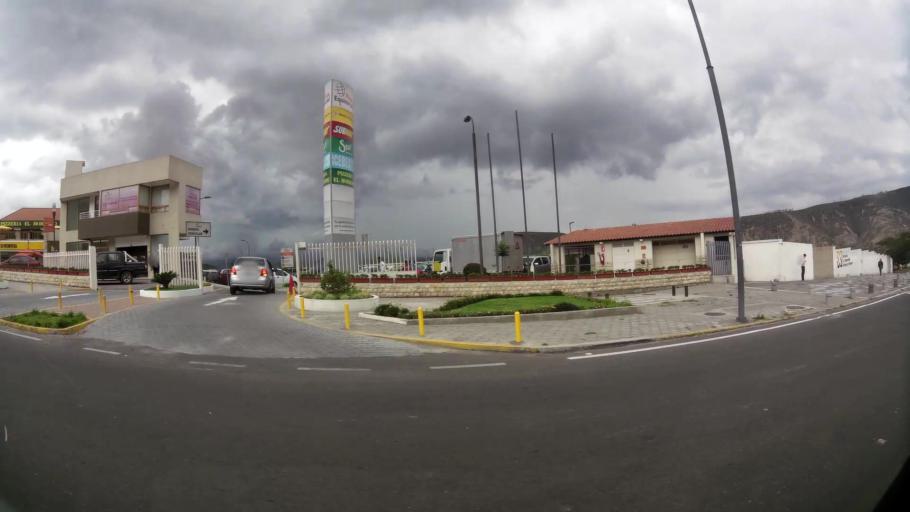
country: EC
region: Pichincha
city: Quito
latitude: -0.0036
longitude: -78.4528
